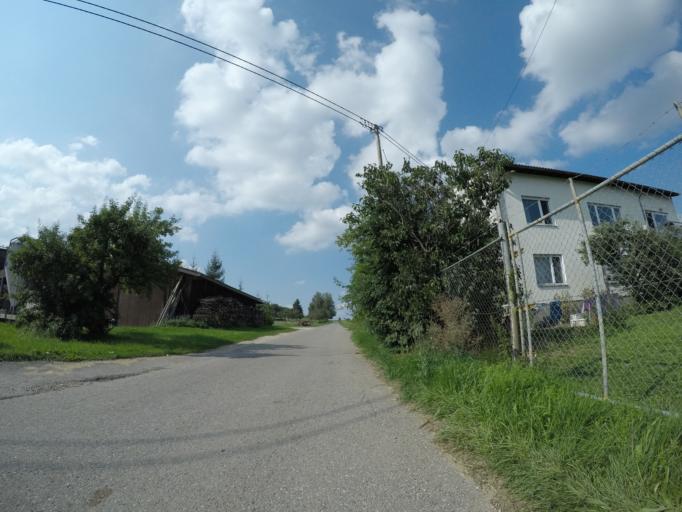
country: DE
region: Baden-Wuerttemberg
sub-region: Tuebingen Region
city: Pfullingen
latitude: 48.4559
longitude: 9.1958
